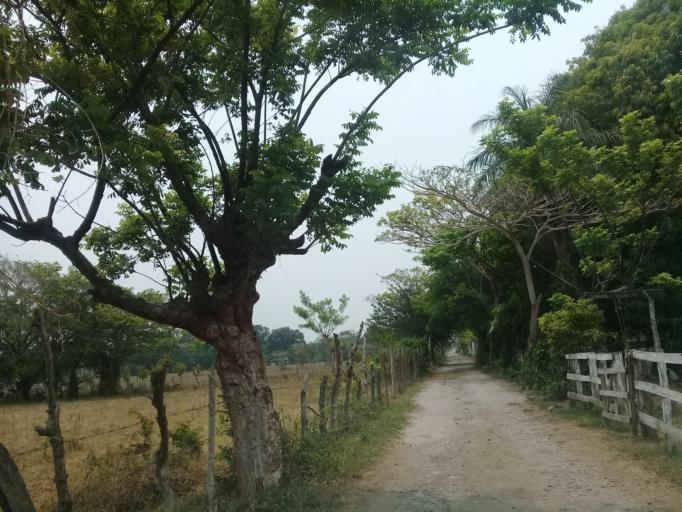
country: MX
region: Veracruz
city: Jamapa
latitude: 18.9585
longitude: -96.1954
